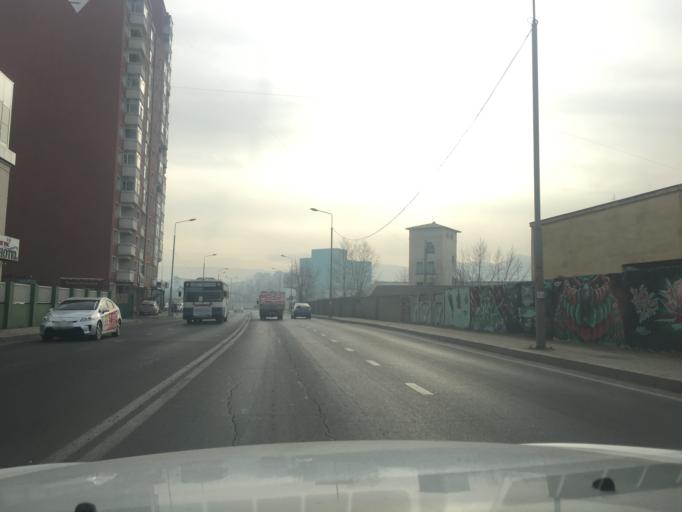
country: MN
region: Ulaanbaatar
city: Ulaanbaatar
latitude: 47.9106
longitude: 106.8750
